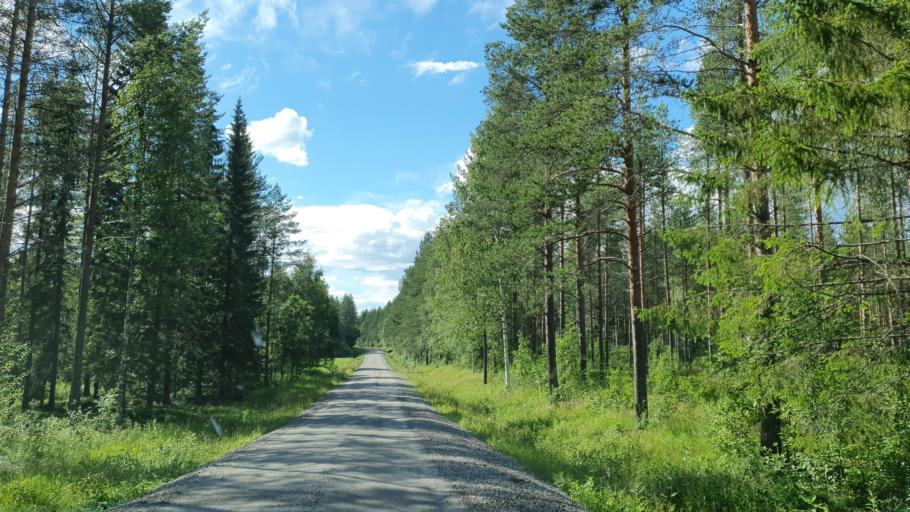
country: FI
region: Kainuu
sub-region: Kehys-Kainuu
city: Kuhmo
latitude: 64.1463
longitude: 29.7690
